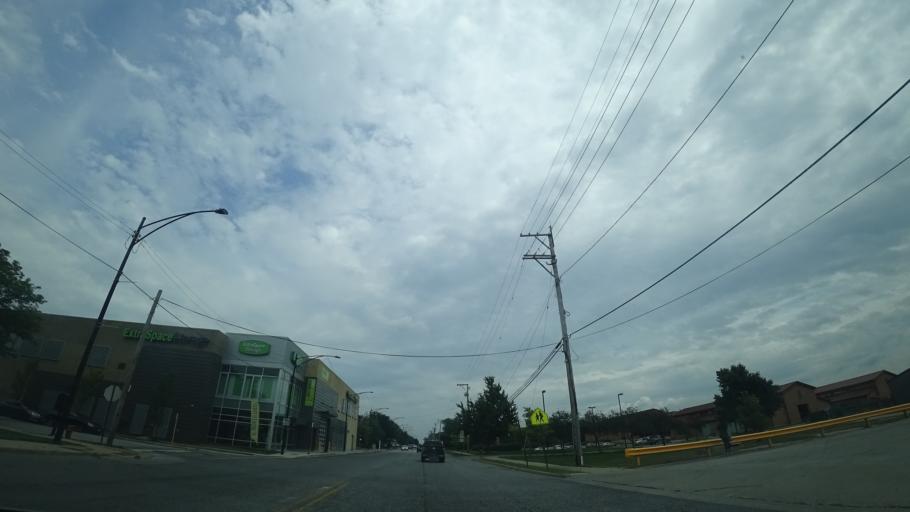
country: US
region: Illinois
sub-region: Cook County
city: Merrionette Park
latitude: 41.6912
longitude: -87.7194
